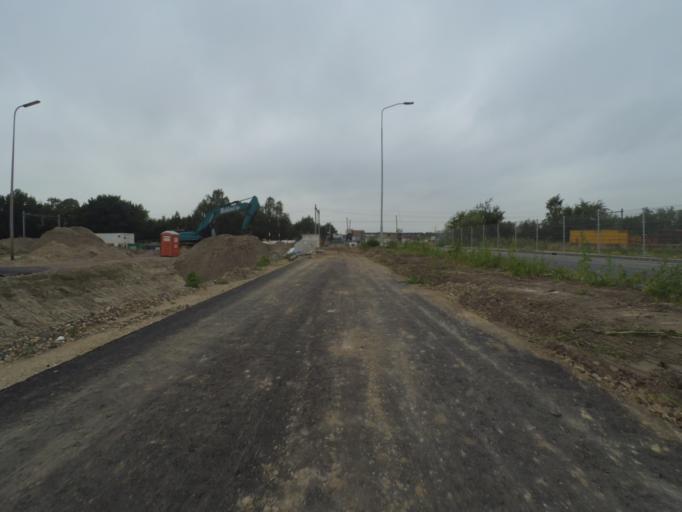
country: NL
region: Gelderland
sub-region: Gemeente Barneveld
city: Voorthuizen
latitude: 52.1653
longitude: 5.6167
